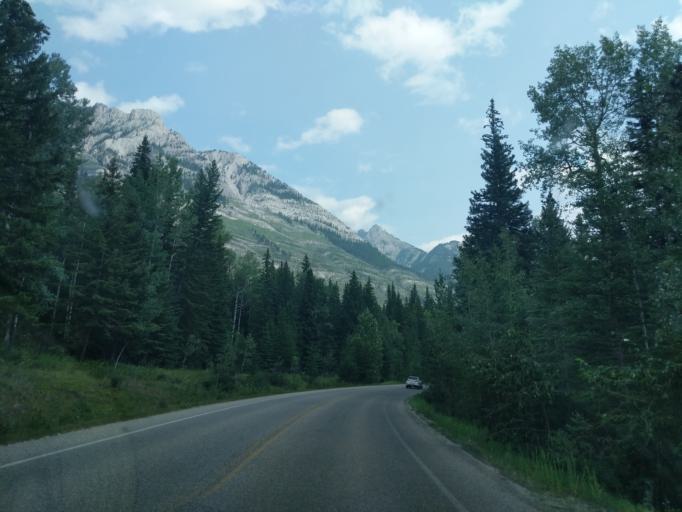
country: CA
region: Alberta
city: Banff
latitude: 51.2147
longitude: -115.7630
